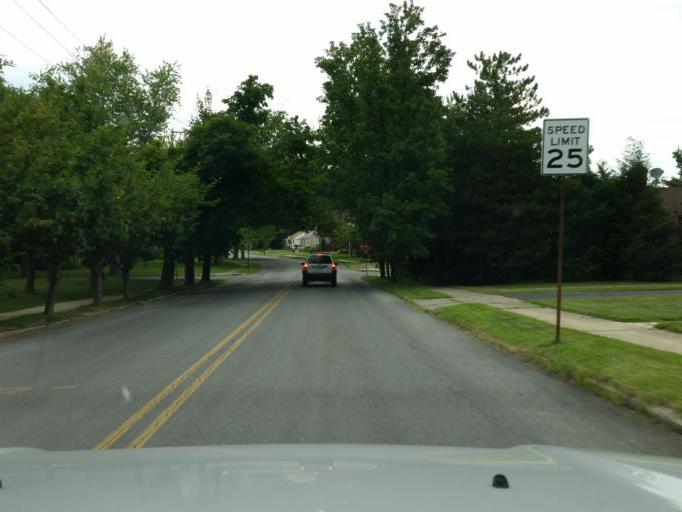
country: US
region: Pennsylvania
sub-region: Blair County
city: Altoona
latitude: 40.5366
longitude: -78.4028
